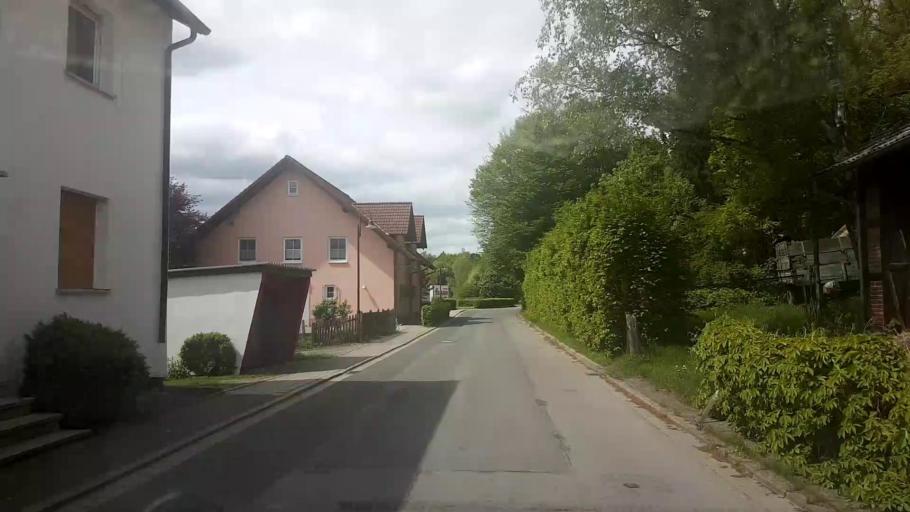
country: DE
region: Bavaria
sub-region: Upper Franconia
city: Untersiemau
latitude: 50.1990
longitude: 10.9914
